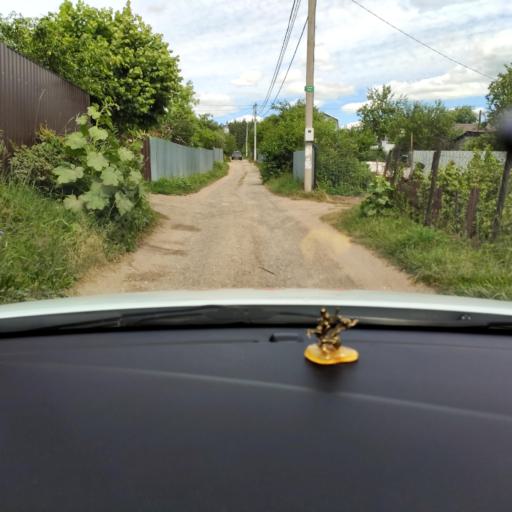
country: RU
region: Tatarstan
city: Staroye Arakchino
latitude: 55.8911
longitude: 49.0430
